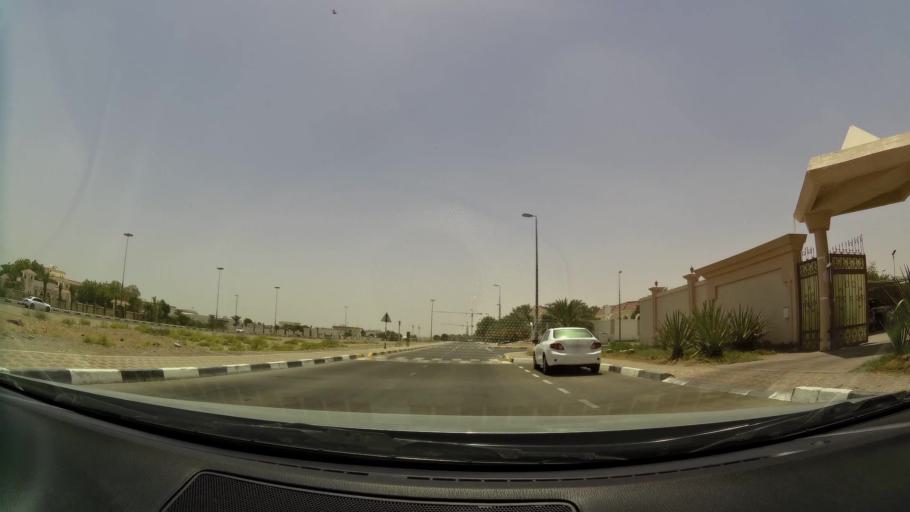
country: OM
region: Al Buraimi
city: Al Buraymi
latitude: 24.2598
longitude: 55.7121
